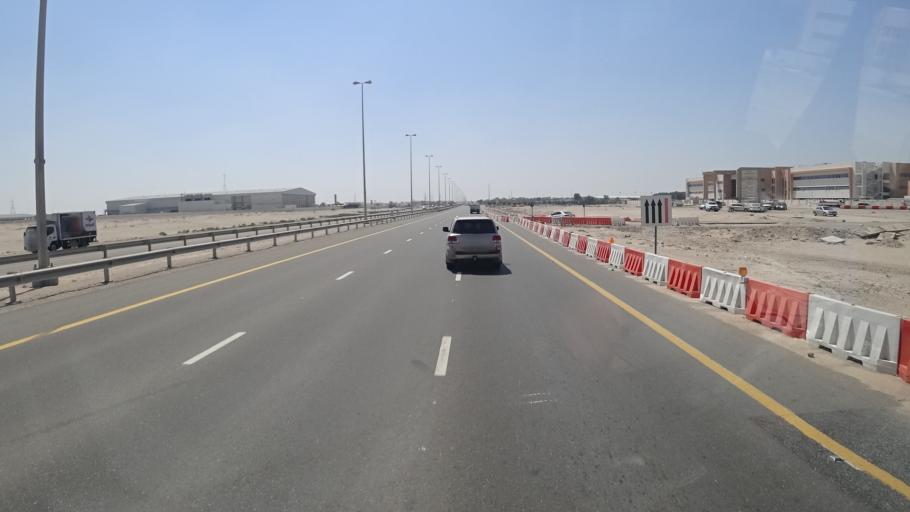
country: AE
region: Abu Dhabi
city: Abu Dhabi
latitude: 24.3129
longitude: 54.6766
